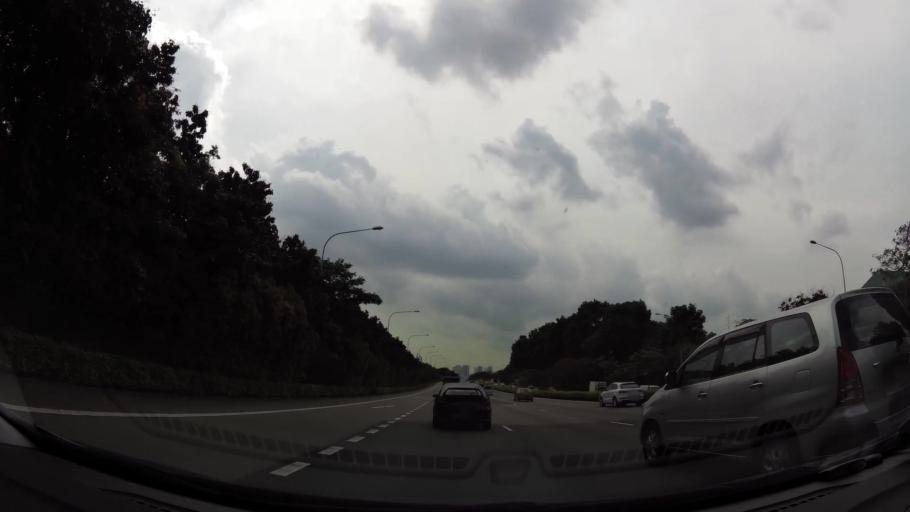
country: MY
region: Johor
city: Kampung Pasir Gudang Baru
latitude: 1.3866
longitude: 103.8584
